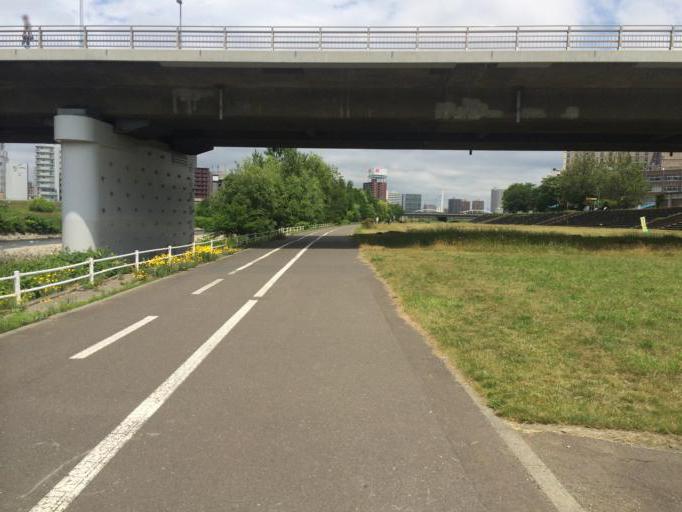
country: JP
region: Hokkaido
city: Sapporo
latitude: 43.0520
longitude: 141.3627
